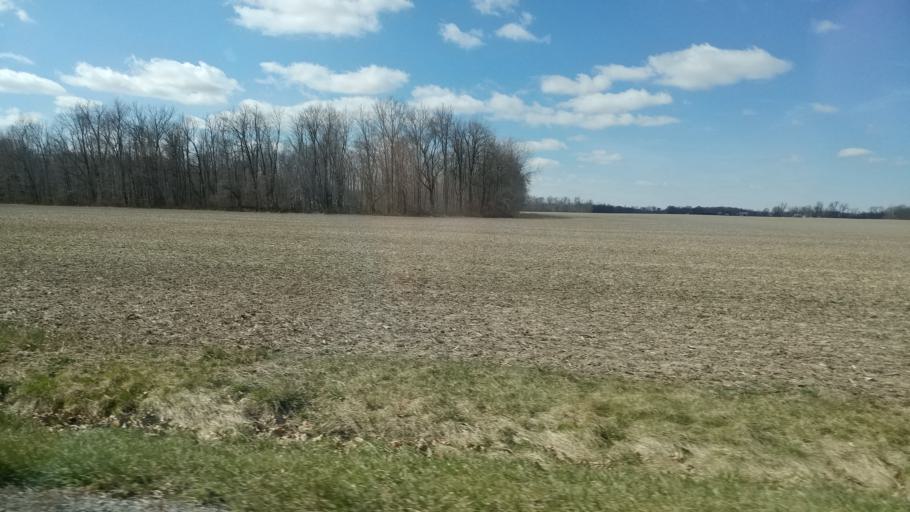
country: US
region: Ohio
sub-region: Wyandot County
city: Carey
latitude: 40.9726
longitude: -83.5128
